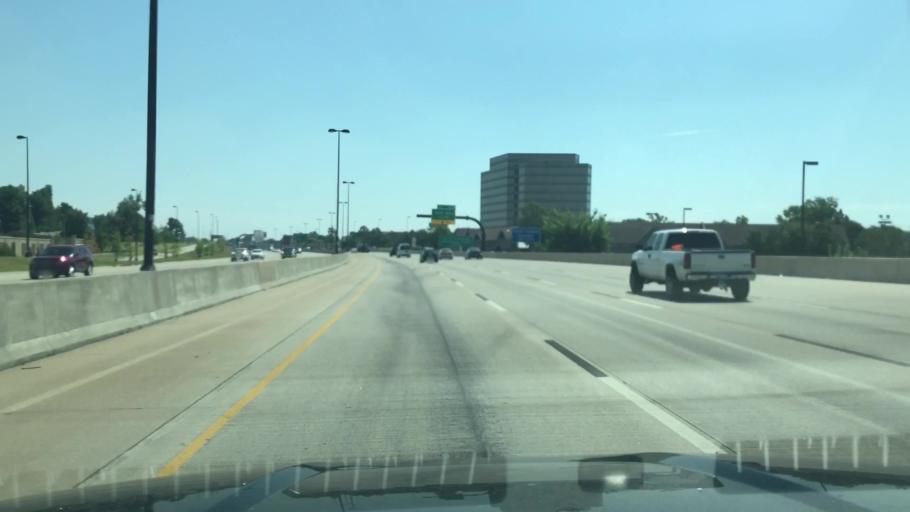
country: US
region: Oklahoma
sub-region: Tulsa County
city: Jenks
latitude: 36.0909
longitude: -95.9334
